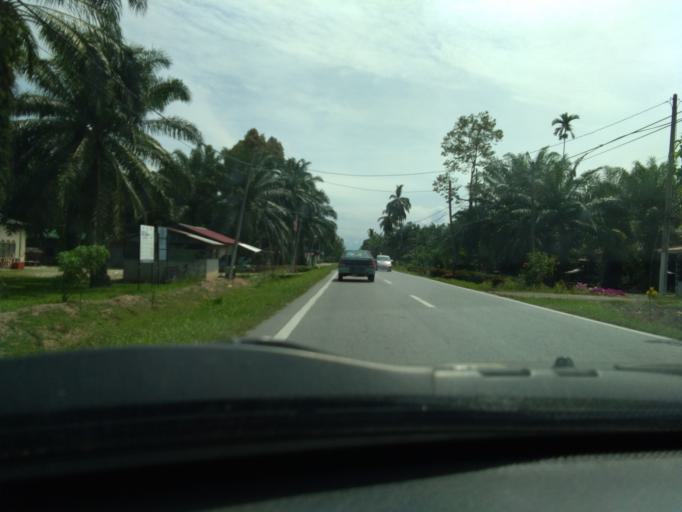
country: MY
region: Perak
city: Bagan Serai
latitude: 5.0354
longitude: 100.5667
